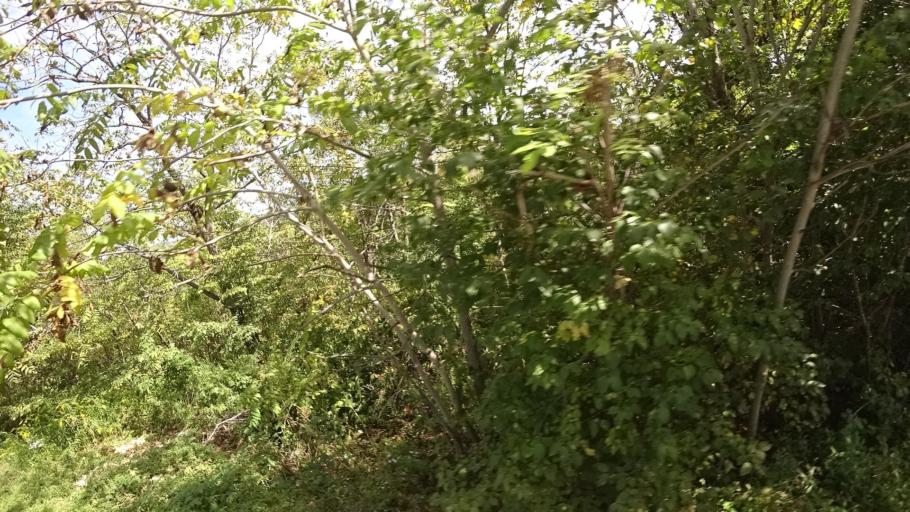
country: RU
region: Primorskiy
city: Yakovlevka
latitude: 44.3927
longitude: 133.6051
